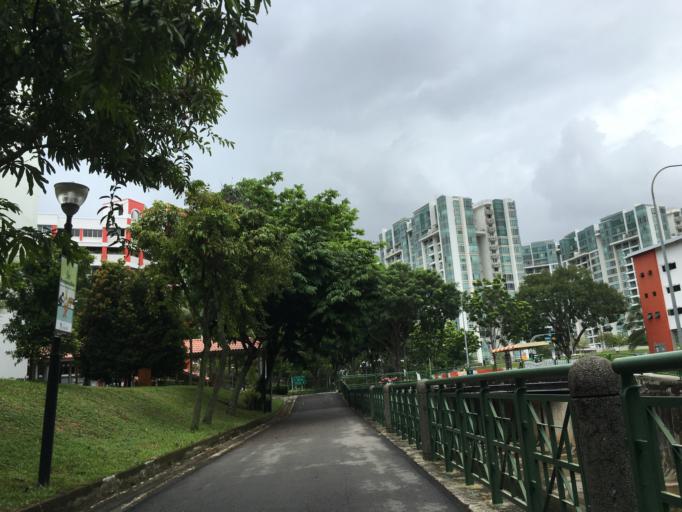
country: MY
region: Johor
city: Kampung Pasir Gudang Baru
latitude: 1.3794
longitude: 103.8958
